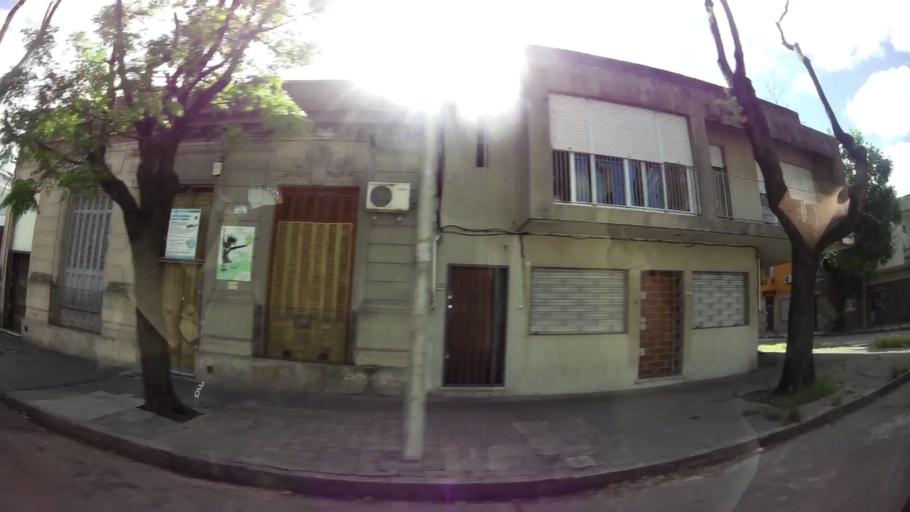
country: UY
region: Montevideo
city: Montevideo
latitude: -34.8761
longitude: -56.1773
